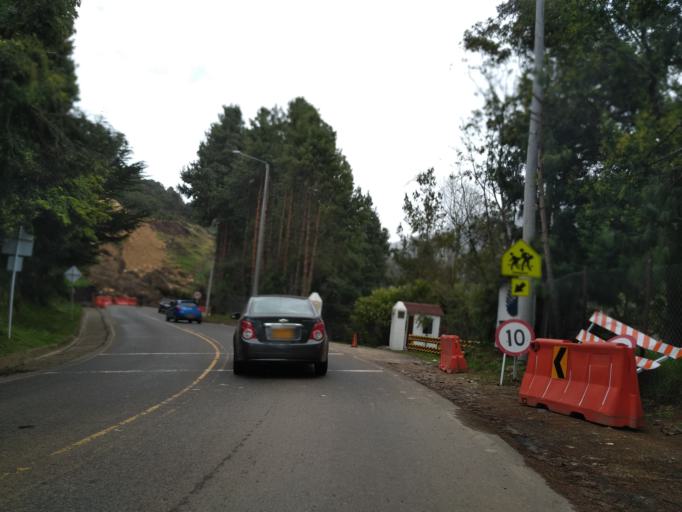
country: CO
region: Bogota D.C.
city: Barrio San Luis
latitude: 4.6705
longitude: -73.9970
